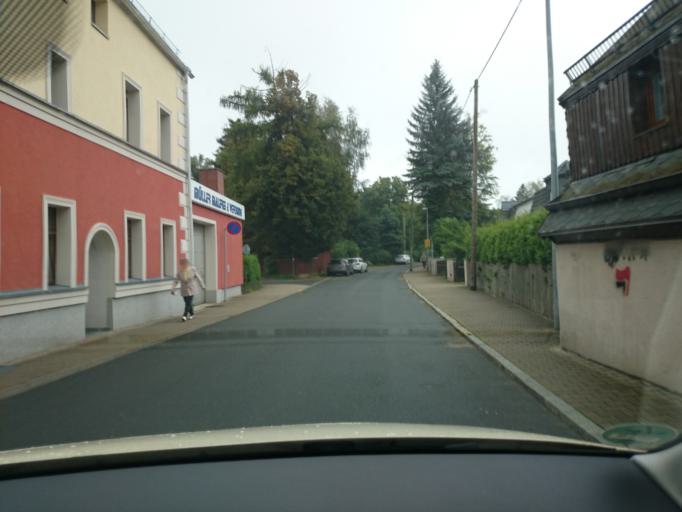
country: DE
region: Saxony
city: Brand-Erbisdorf
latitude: 50.8675
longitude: 13.3206
